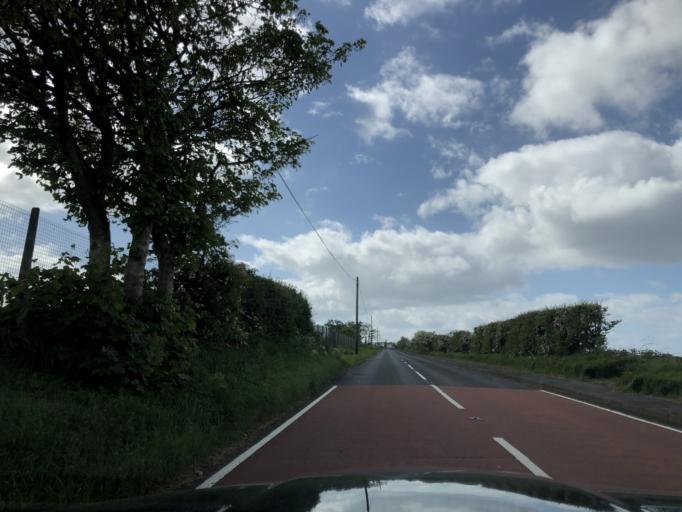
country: GB
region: Northern Ireland
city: Bushmills
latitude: 55.2065
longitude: -6.5325
